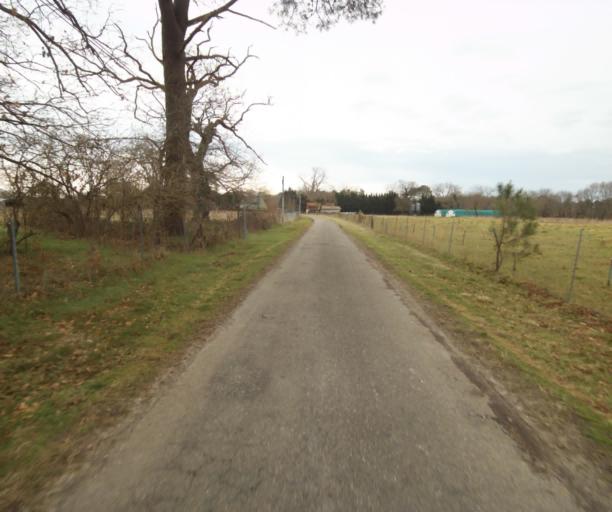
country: FR
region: Aquitaine
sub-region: Departement des Landes
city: Gabarret
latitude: 44.0153
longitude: -0.0573
